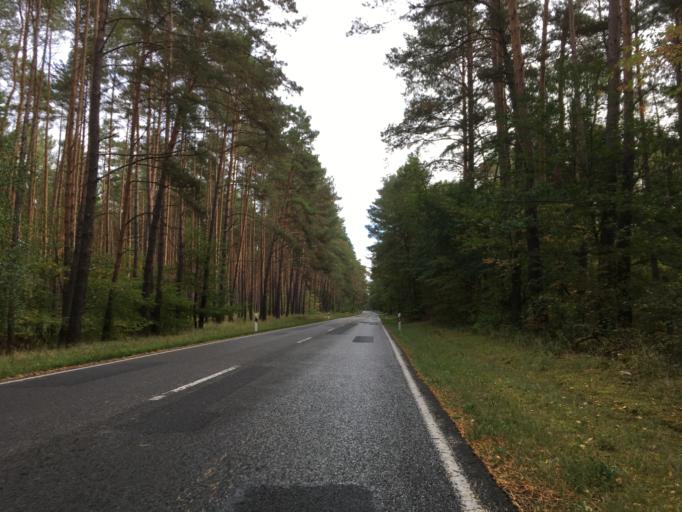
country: DE
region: Brandenburg
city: Oderberg
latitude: 52.8869
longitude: 14.1003
